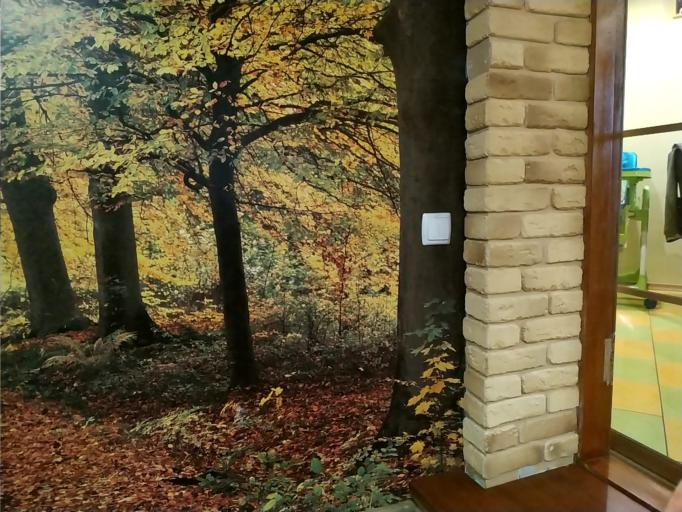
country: RU
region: Smolensk
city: Safonovo
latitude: 55.1950
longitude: 33.1436
